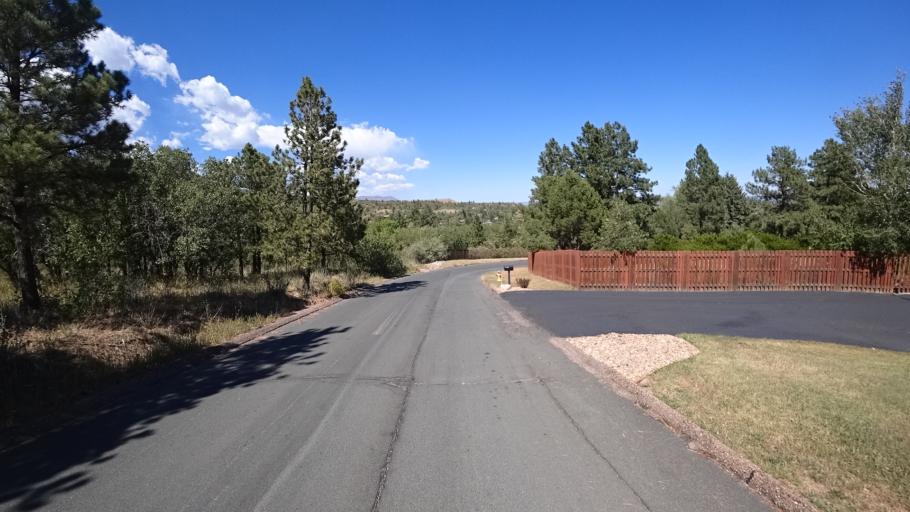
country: US
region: Colorado
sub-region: El Paso County
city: Colorado Springs
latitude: 38.7869
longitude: -104.8637
